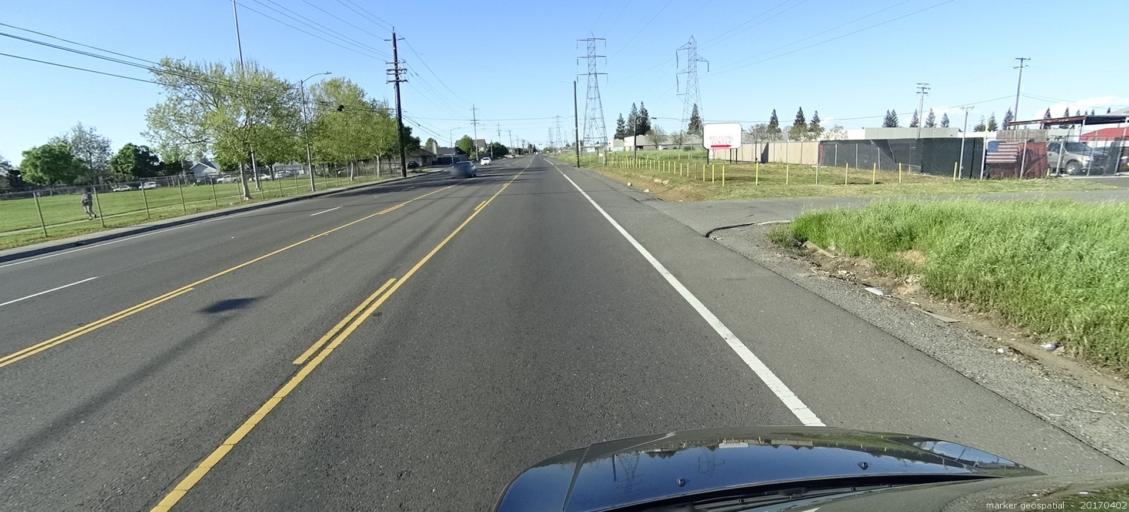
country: US
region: California
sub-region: Sacramento County
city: Florin
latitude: 38.5026
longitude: -121.4090
